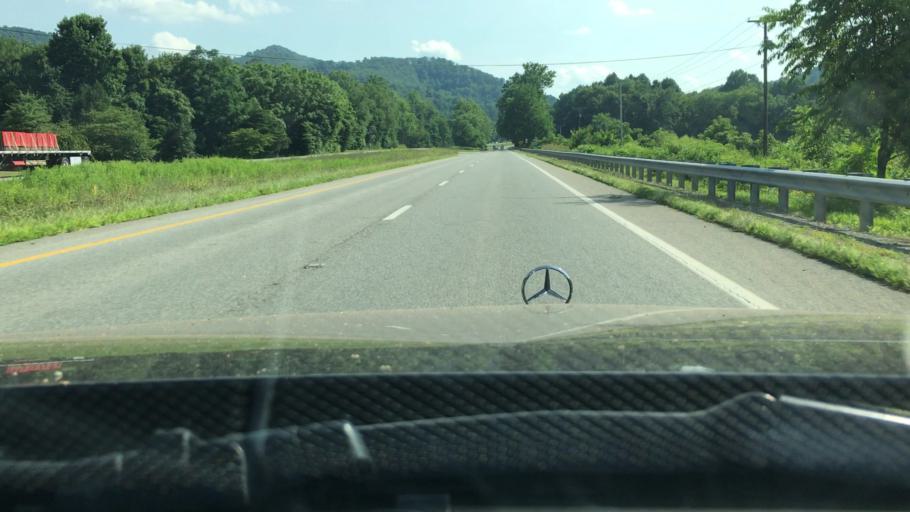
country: US
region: Virginia
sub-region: Albemarle County
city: Crozet
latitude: 37.8999
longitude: -78.6954
